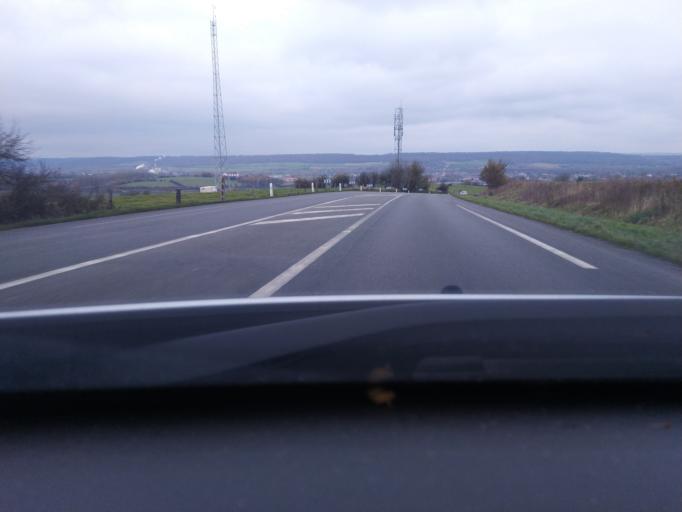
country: FR
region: Nord-Pas-de-Calais
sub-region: Departement du Pas-de-Calais
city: Hesdin
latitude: 50.3542
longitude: 2.0346
